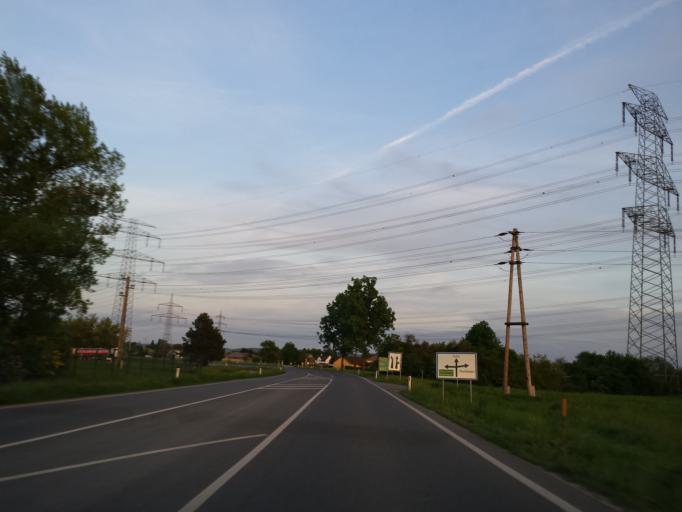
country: AT
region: Lower Austria
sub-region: Politischer Bezirk Tulln
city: Michelhausen
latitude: 48.3330
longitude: 15.9435
